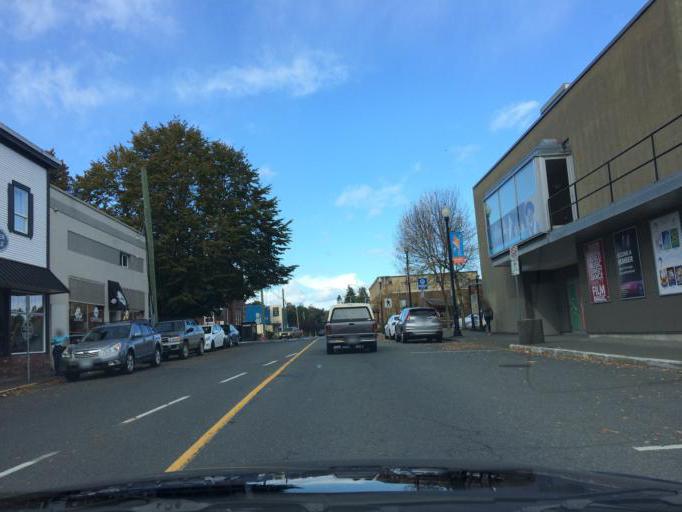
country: CA
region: British Columbia
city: Courtenay
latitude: 49.6917
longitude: -124.9974
